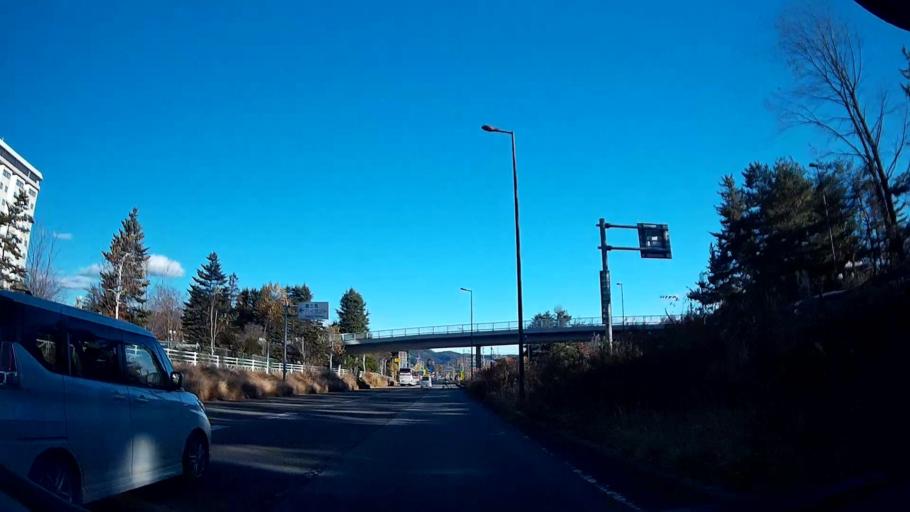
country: JP
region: Yamanashi
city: Fujikawaguchiko
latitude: 35.4839
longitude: 138.7771
